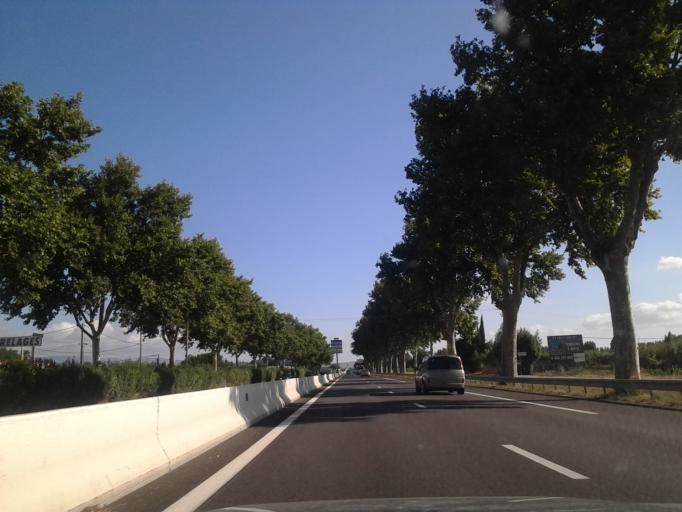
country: FR
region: Languedoc-Roussillon
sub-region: Departement des Pyrenees-Orientales
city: Rivesaltes
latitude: 42.7633
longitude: 2.8986
